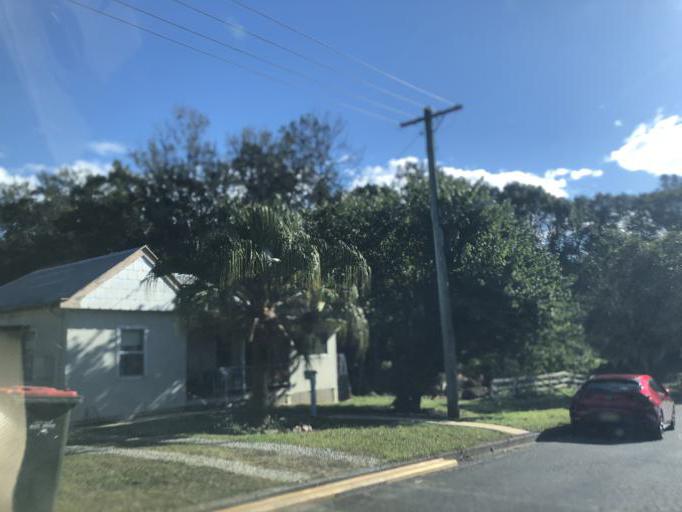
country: AU
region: New South Wales
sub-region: Nambucca Shire
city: Bowraville
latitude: -30.6469
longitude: 152.8514
